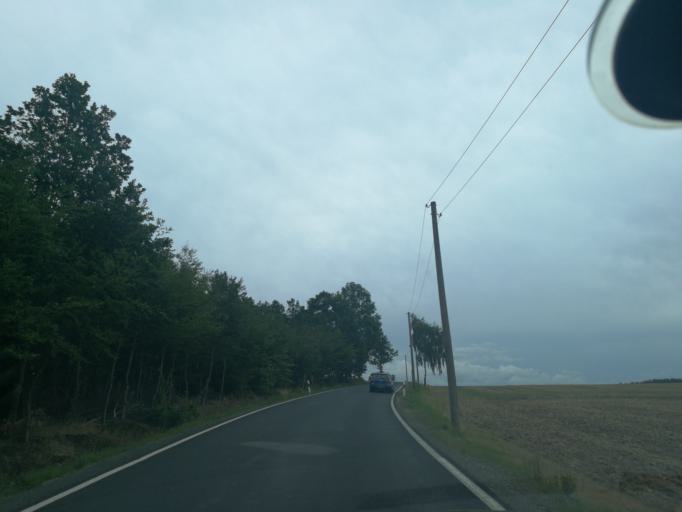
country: DE
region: Saxony
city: Triebel
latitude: 50.3344
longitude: 12.1182
